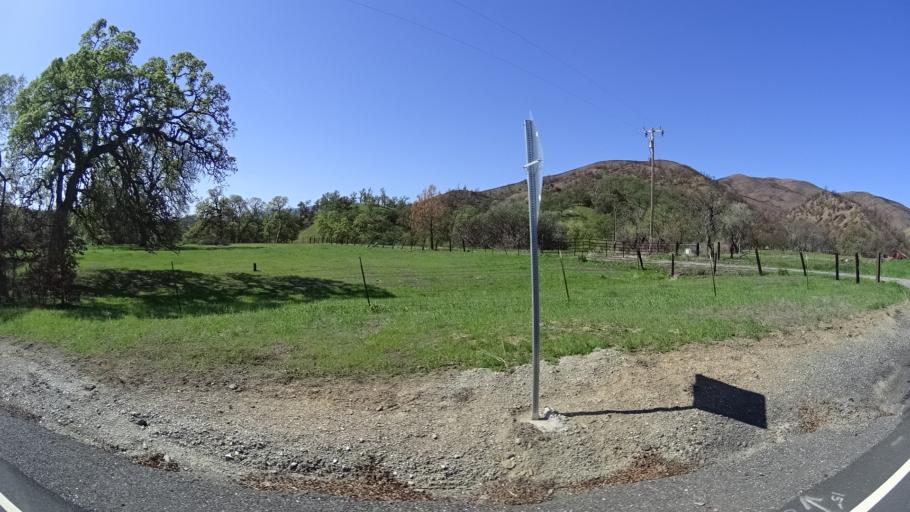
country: US
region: California
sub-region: Glenn County
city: Orland
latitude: 39.6556
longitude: -122.5893
